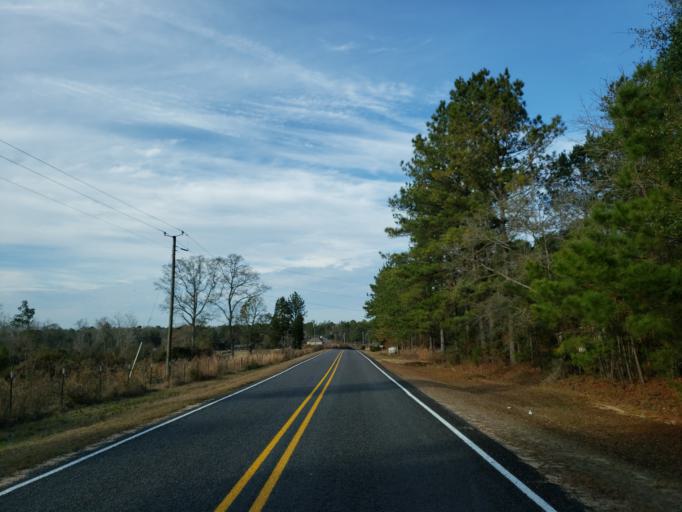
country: US
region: Mississippi
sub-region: Wayne County
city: Belmont
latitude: 31.4977
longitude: -88.5063
